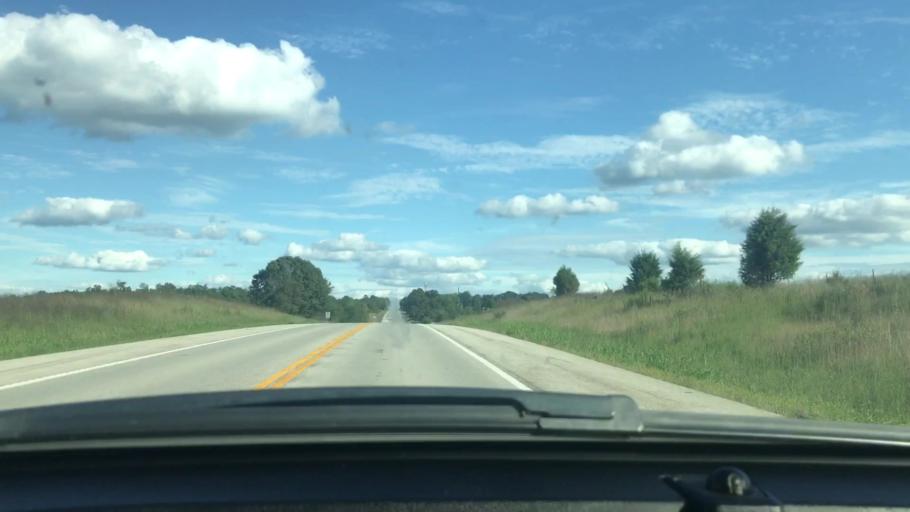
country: US
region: Missouri
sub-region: Howell County
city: West Plains
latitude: 36.6567
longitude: -91.7006
